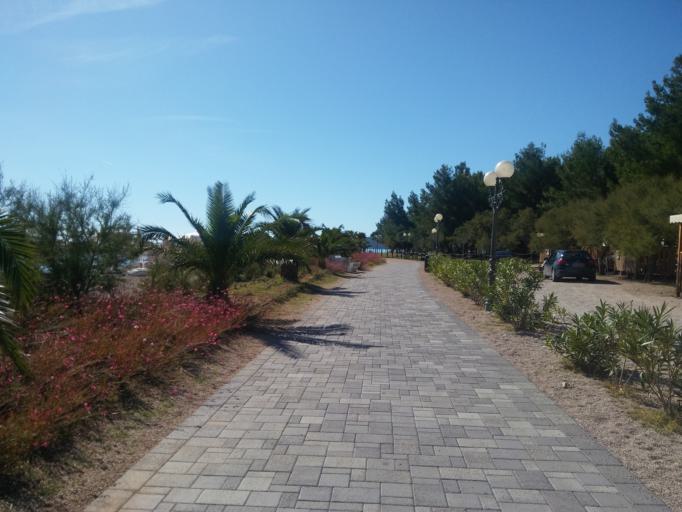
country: HR
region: Sibensko-Kniniska
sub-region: Grad Sibenik
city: Brodarica
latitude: 43.6960
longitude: 15.8907
